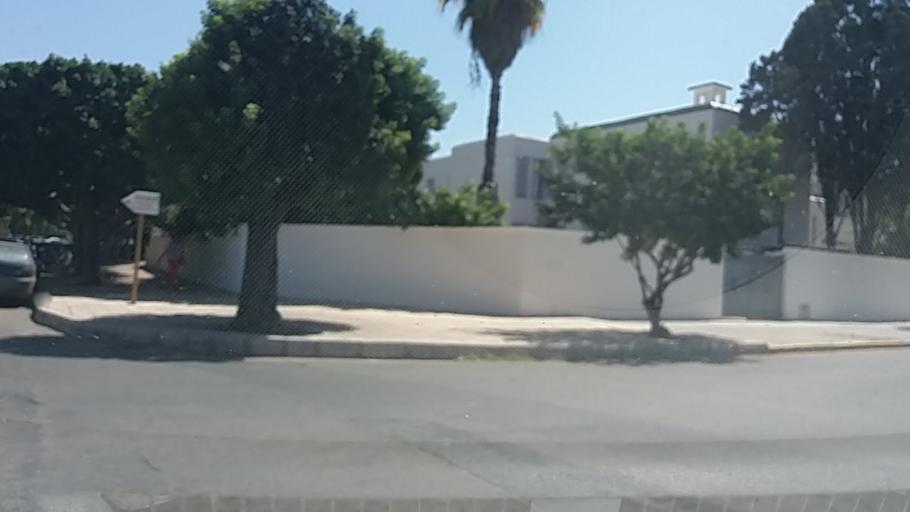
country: MA
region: Rabat-Sale-Zemmour-Zaer
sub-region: Rabat
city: Rabat
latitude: 34.0148
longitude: -6.8266
